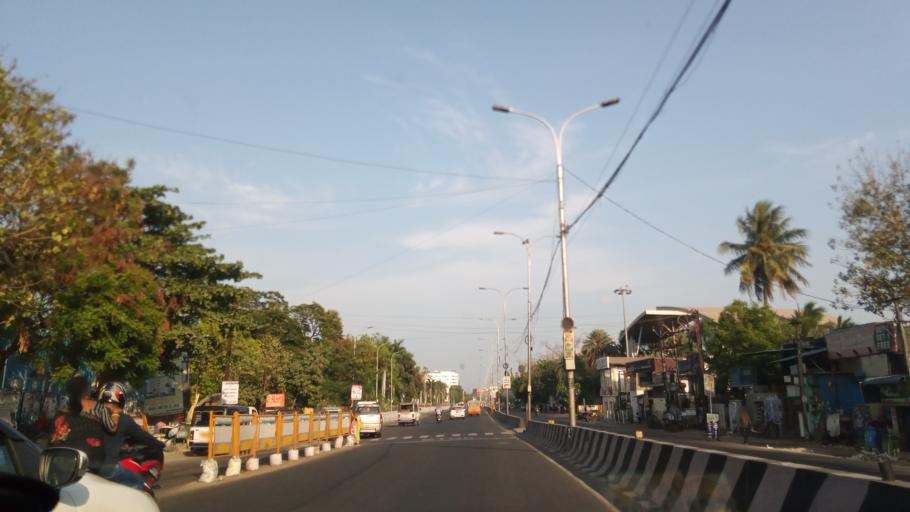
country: IN
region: Tamil Nadu
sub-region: Kancheepuram
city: Manappakkam
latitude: 13.0251
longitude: 80.1765
